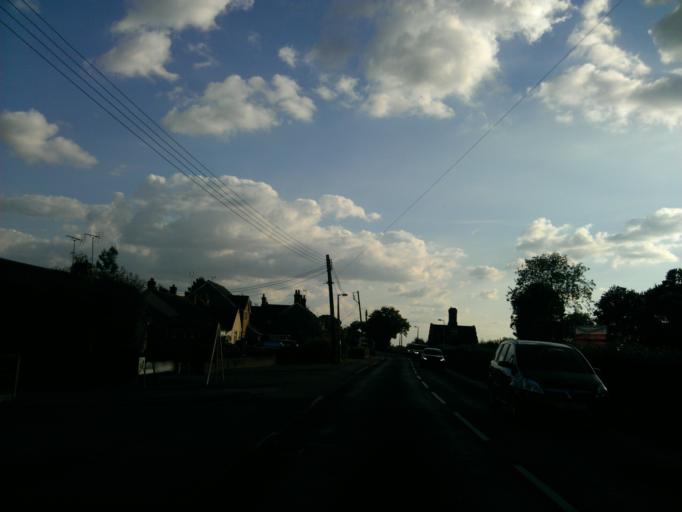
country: GB
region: England
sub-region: Essex
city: Braintree
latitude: 51.9037
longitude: 0.5723
